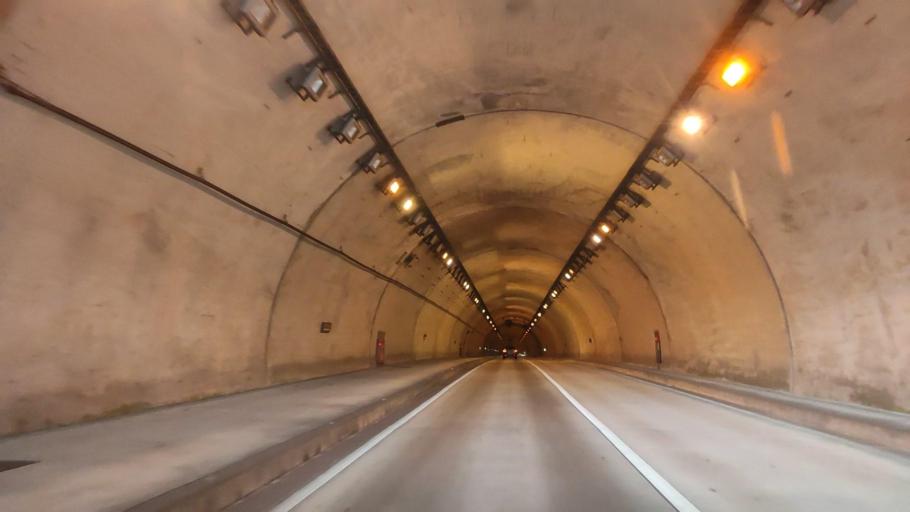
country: JP
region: Ehime
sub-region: Shikoku-chuo Shi
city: Matsuyama
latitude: 33.8761
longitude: 132.7143
